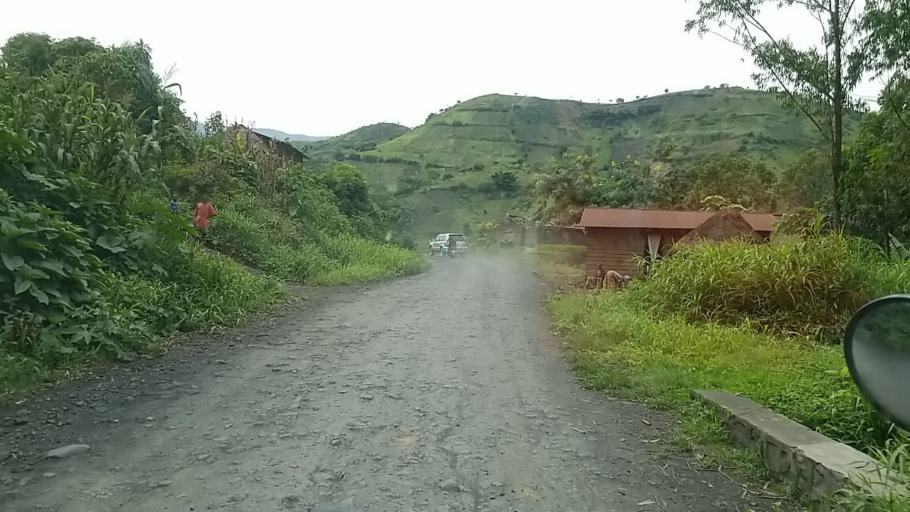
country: CD
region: Nord Kivu
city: Sake
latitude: -1.7380
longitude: 29.0039
